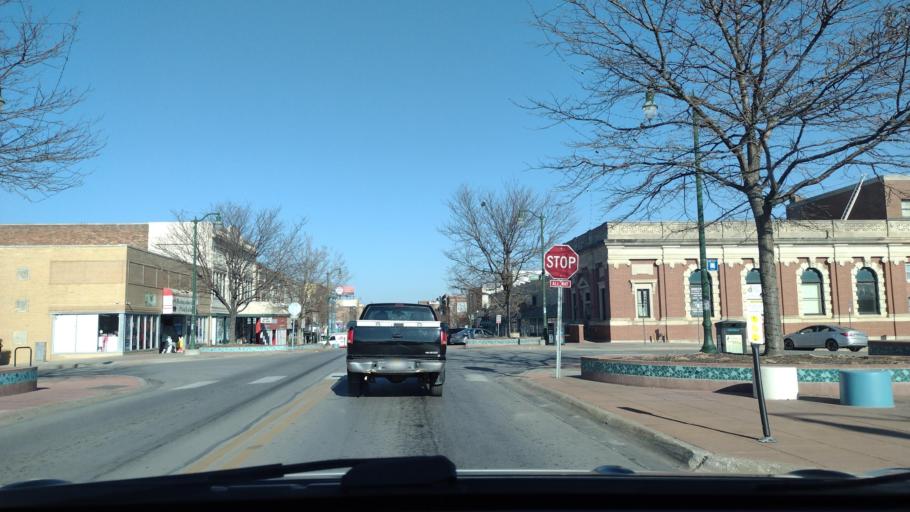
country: US
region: Nebraska
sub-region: Douglas County
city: Omaha
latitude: 41.2080
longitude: -95.9470
